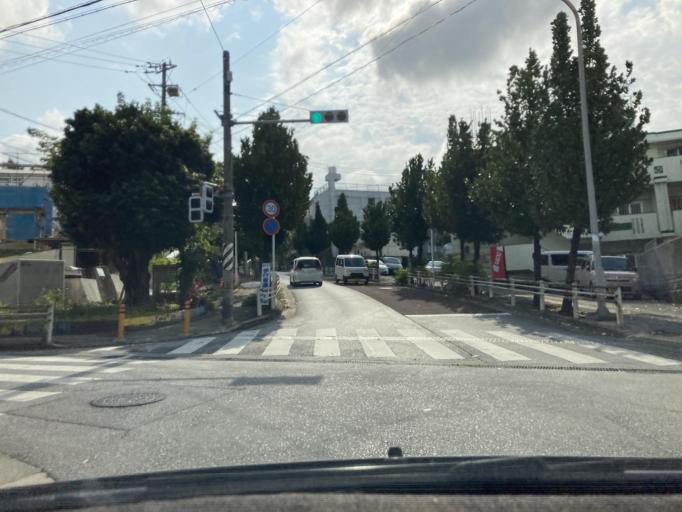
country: JP
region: Okinawa
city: Tomigusuku
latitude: 26.1991
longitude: 127.7184
